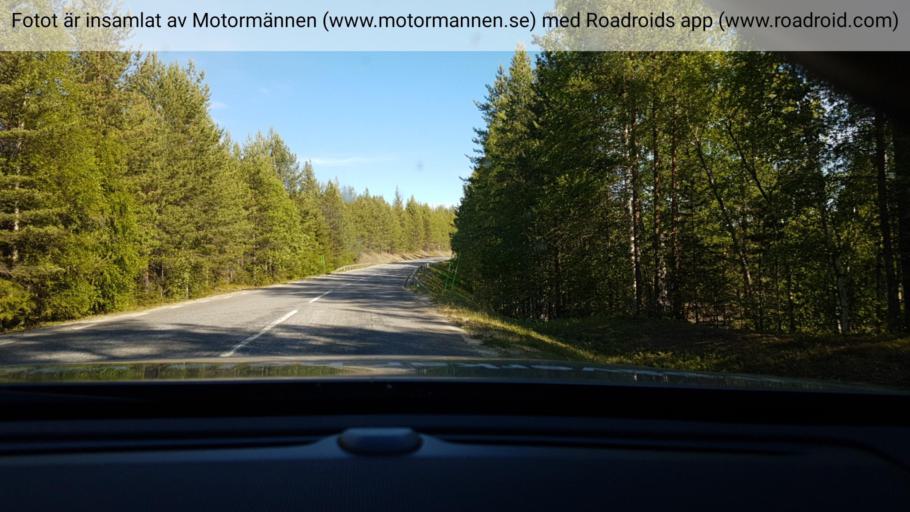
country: SE
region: Vaesterbotten
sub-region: Lycksele Kommun
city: Lycksele
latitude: 64.7798
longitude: 19.0040
